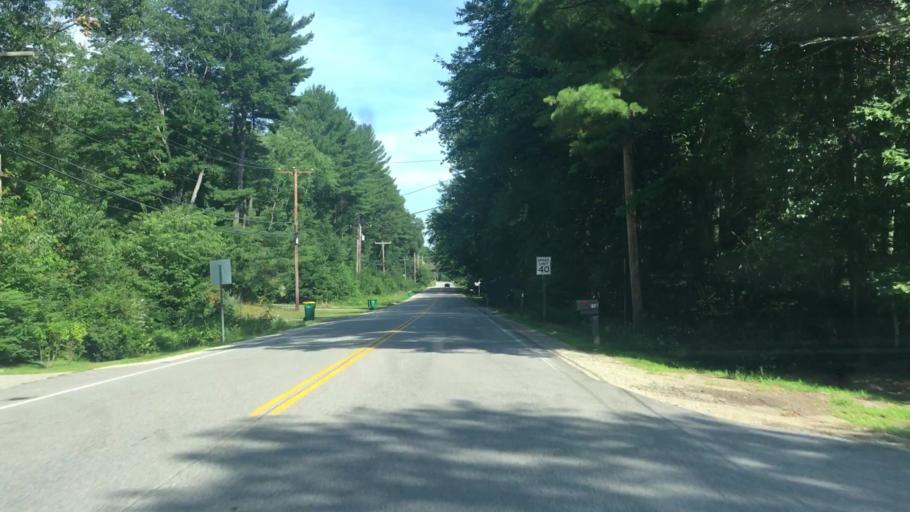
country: US
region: New Hampshire
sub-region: Strafford County
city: Rochester
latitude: 43.2704
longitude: -70.9489
